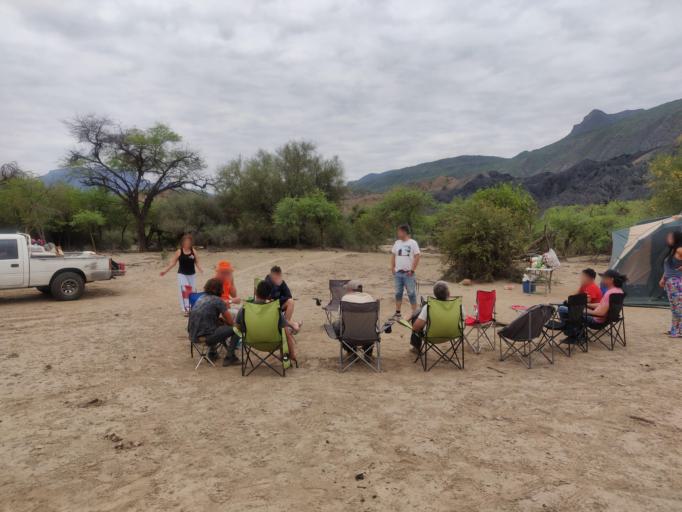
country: BO
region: Chuquisaca
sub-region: Provincia Zudanez
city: Mojocoya
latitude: -18.5403
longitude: -64.5542
